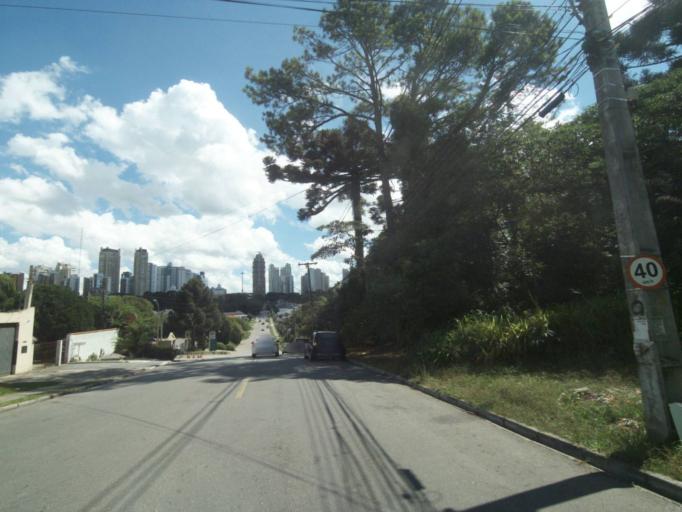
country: BR
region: Parana
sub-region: Curitiba
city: Curitiba
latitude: -25.4315
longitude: -49.3340
